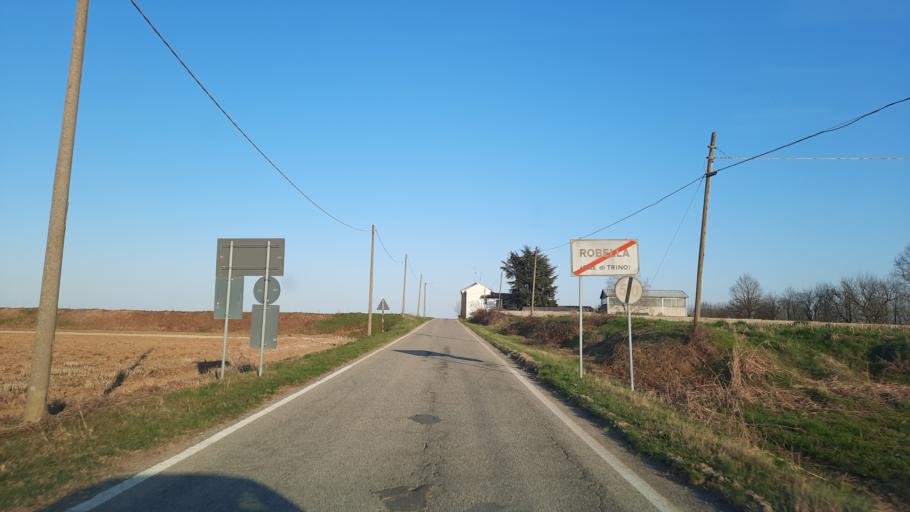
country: IT
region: Piedmont
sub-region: Provincia di Vercelli
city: Tricerro
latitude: 45.2047
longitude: 8.3376
